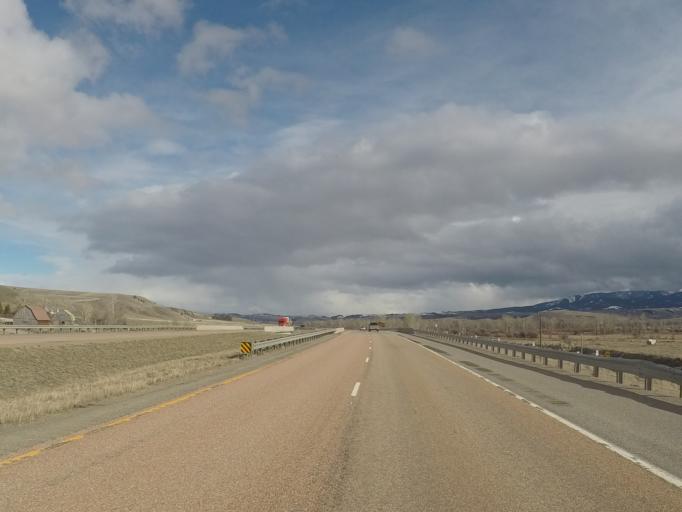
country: US
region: Montana
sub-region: Granite County
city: Philipsburg
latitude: 46.6487
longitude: -113.1197
